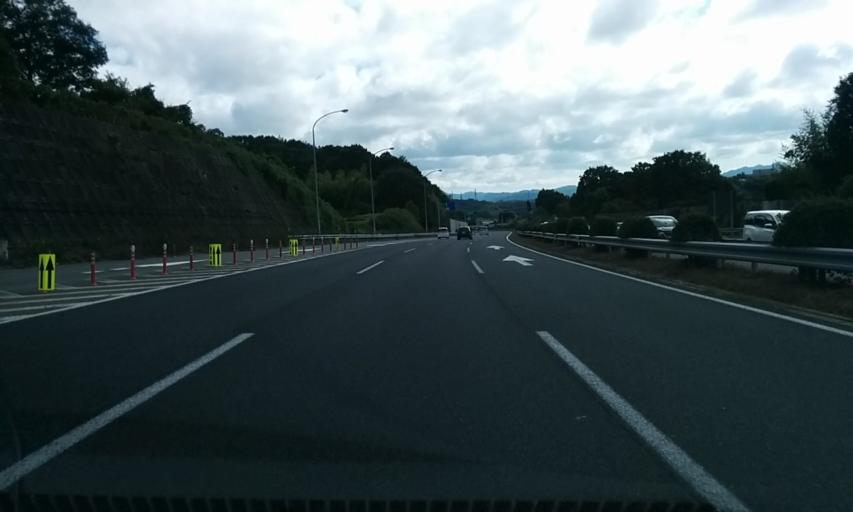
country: JP
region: Hyogo
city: Sandacho
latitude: 34.8852
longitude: 135.1716
